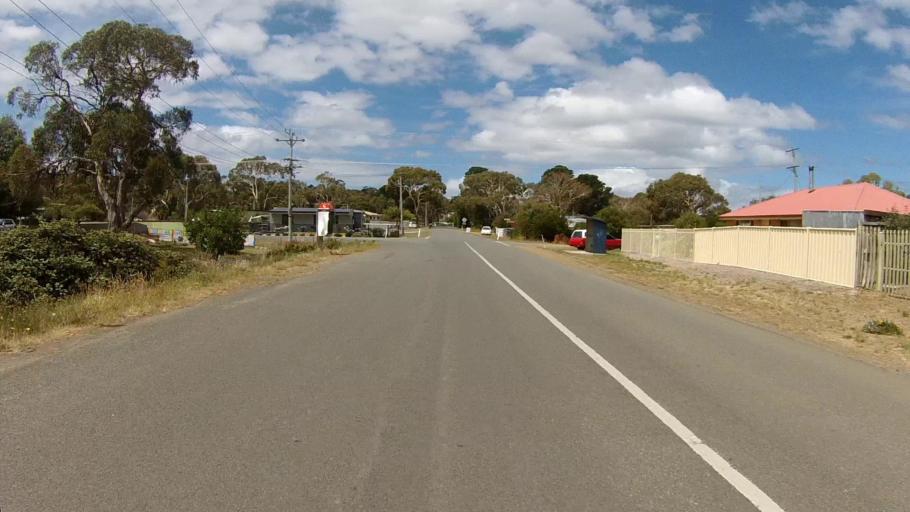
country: AU
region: Tasmania
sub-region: Sorell
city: Sorell
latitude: -42.8706
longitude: 147.6382
